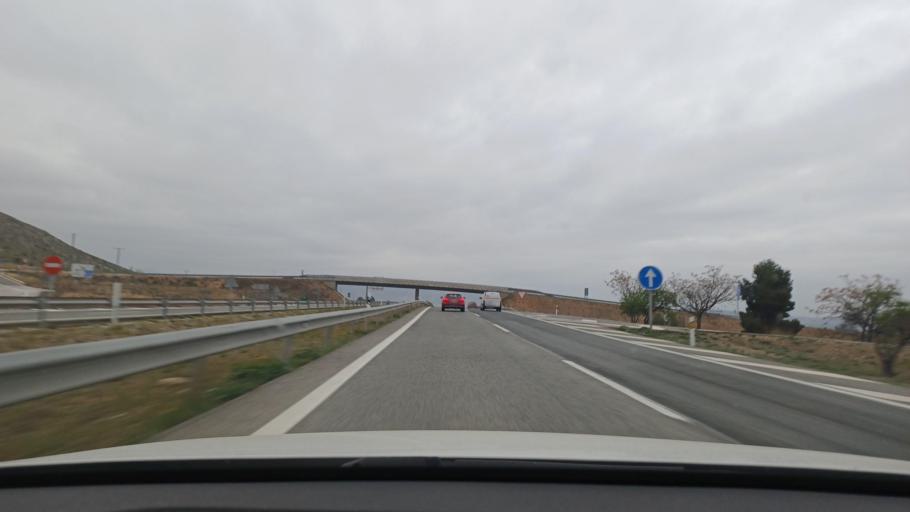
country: ES
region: Castille-La Mancha
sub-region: Provincia de Albacete
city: Caudete
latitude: 38.6973
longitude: -0.9171
